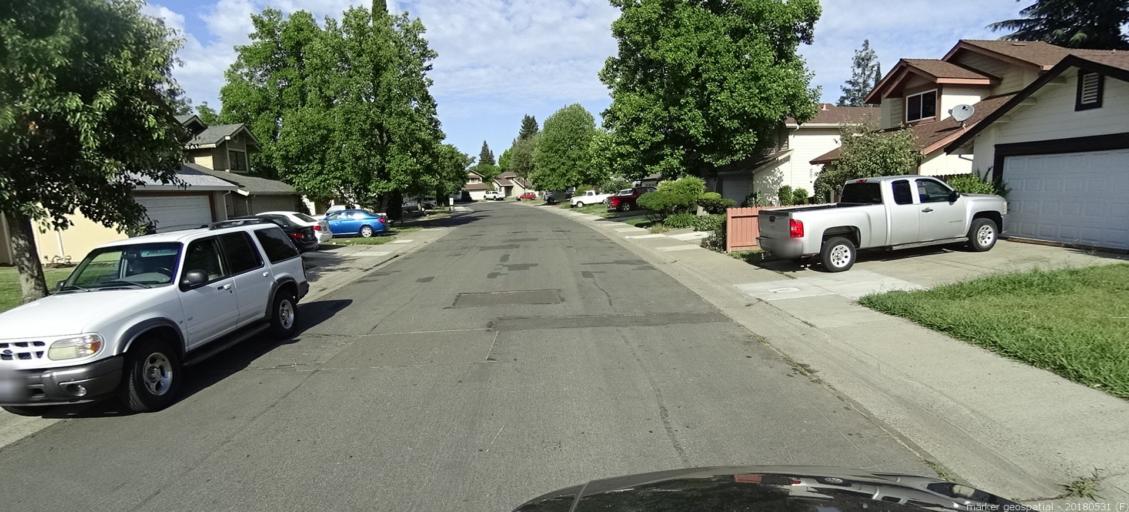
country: US
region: California
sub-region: Sacramento County
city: Sacramento
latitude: 38.6332
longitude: -121.4865
